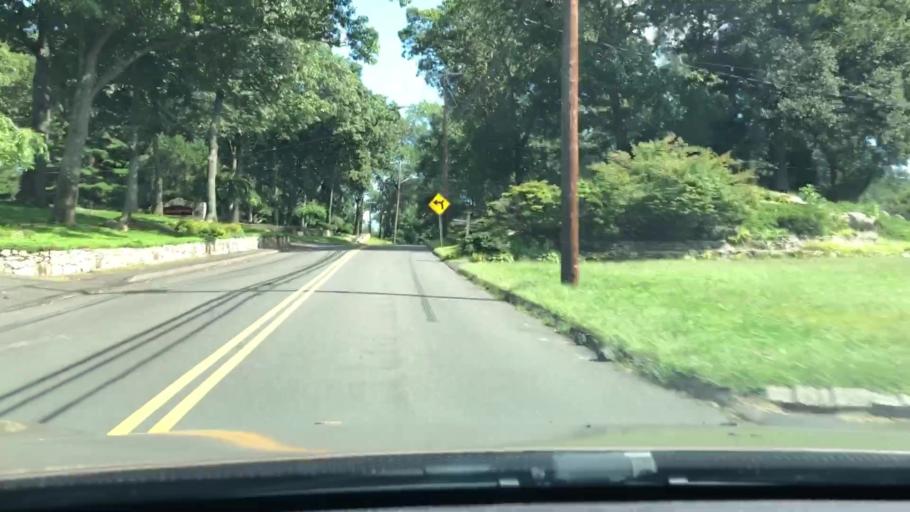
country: US
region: Connecticut
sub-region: Fairfield County
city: Darien
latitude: 41.1096
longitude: -73.4493
